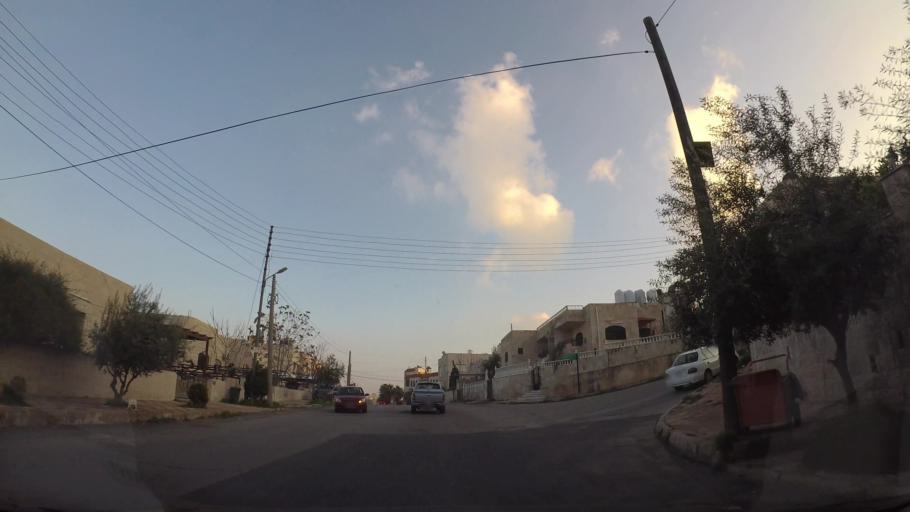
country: JO
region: Amman
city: Amman
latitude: 31.9987
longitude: 35.9504
